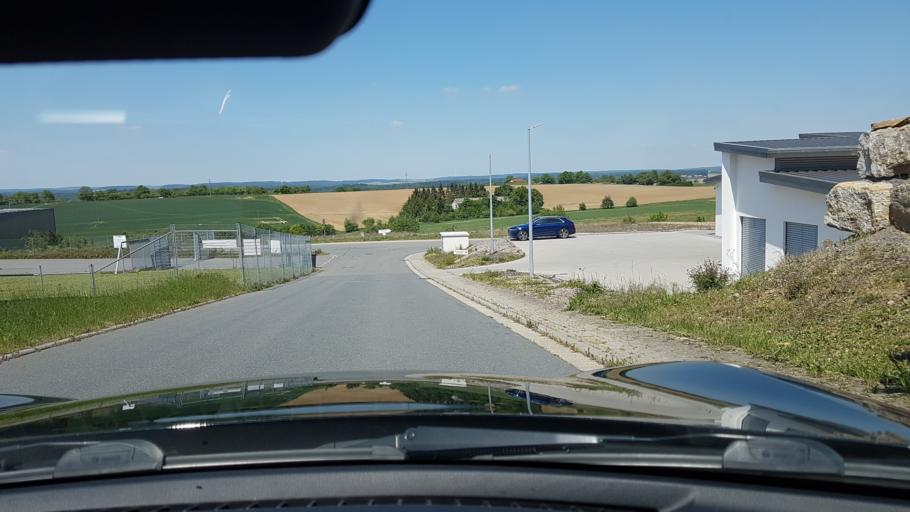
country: DE
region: Baden-Wuerttemberg
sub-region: Karlsruhe Region
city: Osterburken
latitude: 49.4237
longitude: 9.4490
